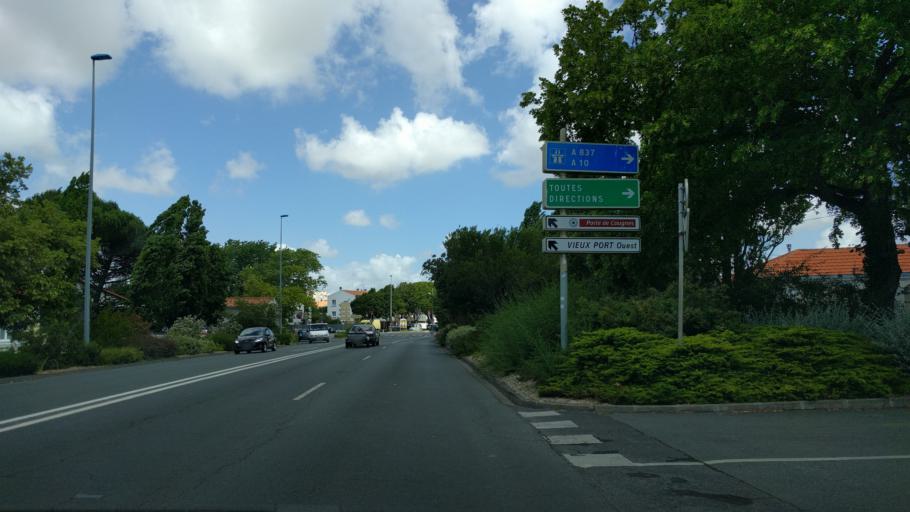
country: FR
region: Poitou-Charentes
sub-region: Departement de la Charente-Maritime
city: La Rochelle
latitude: 46.1655
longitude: -1.1367
